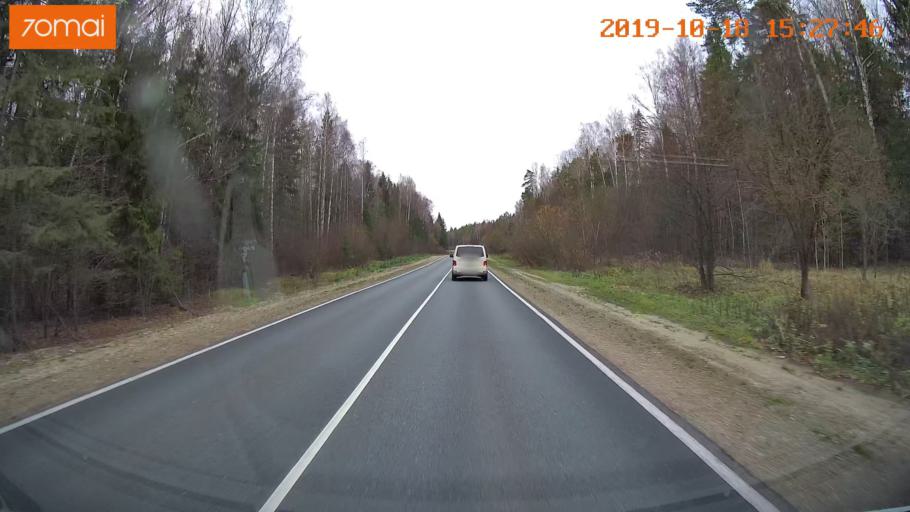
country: RU
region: Vladimir
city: Anopino
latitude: 55.7578
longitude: 40.6723
